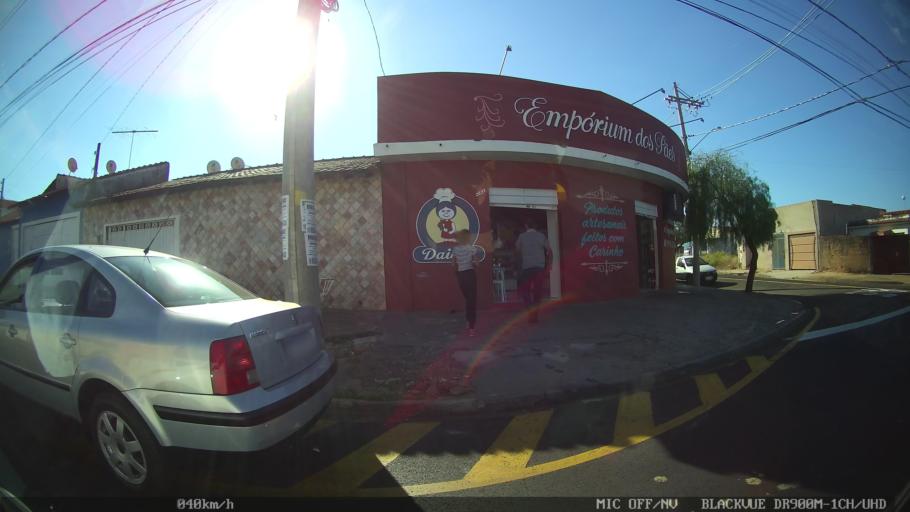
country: BR
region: Sao Paulo
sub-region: Franca
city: Franca
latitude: -20.5097
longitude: -47.4173
